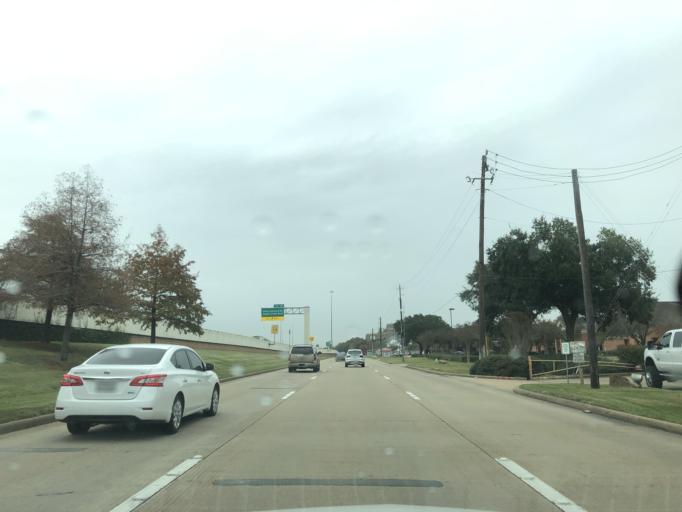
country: US
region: Texas
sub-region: Fort Bend County
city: Sugar Land
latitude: 29.6080
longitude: -95.6121
